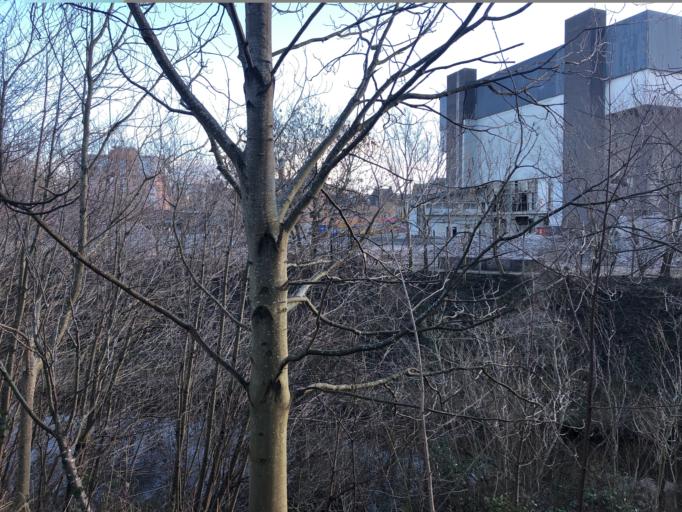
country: GB
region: Scotland
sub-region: Edinburgh
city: Edinburgh
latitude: 55.9682
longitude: -3.1899
